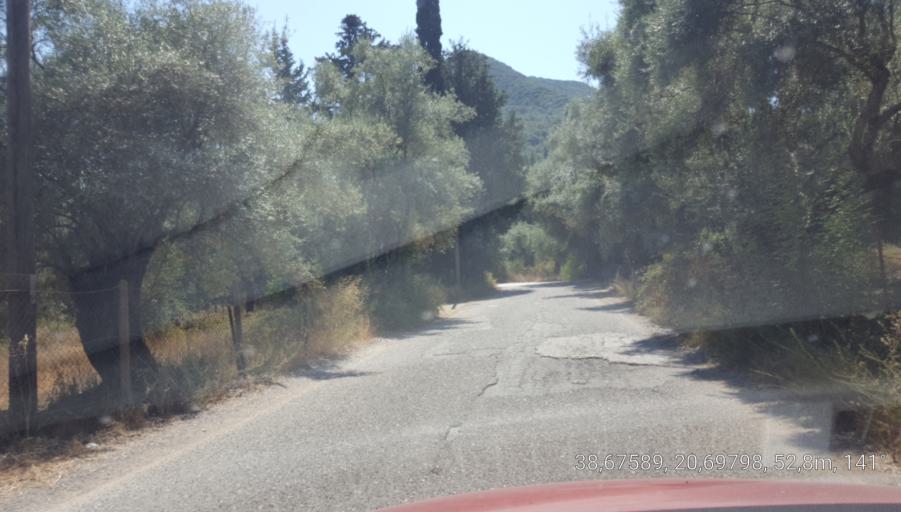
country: GR
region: Ionian Islands
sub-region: Lefkada
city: Nidri
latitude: 38.6758
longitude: 20.6981
